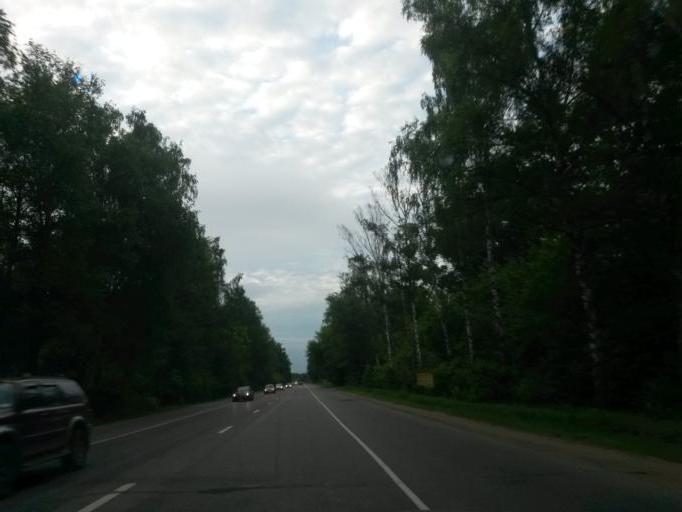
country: RU
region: Moskovskaya
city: Stolbovaya
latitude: 55.2349
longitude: 37.5041
